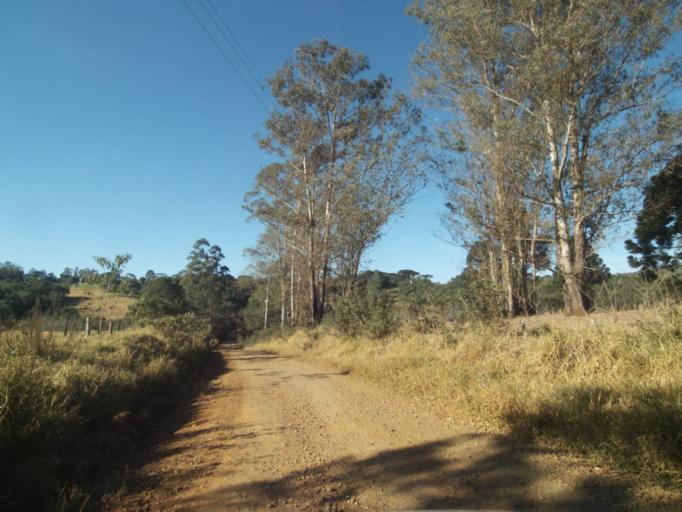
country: BR
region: Parana
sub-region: Tibagi
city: Tibagi
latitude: -24.5417
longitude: -50.5044
